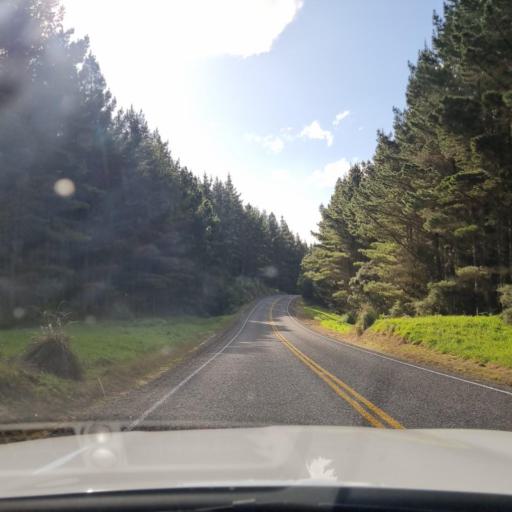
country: NZ
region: Northland
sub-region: Kaipara District
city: Dargaville
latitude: -36.2724
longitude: 174.0545
